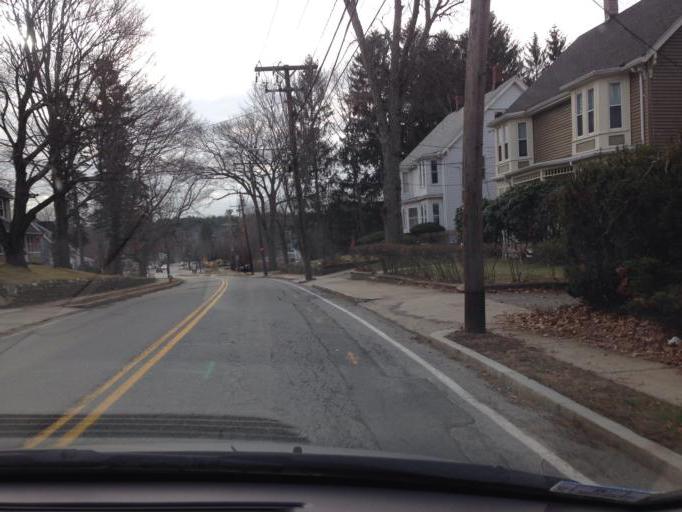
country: US
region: Massachusetts
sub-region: Middlesex County
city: Bedford
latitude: 42.4876
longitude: -71.2786
